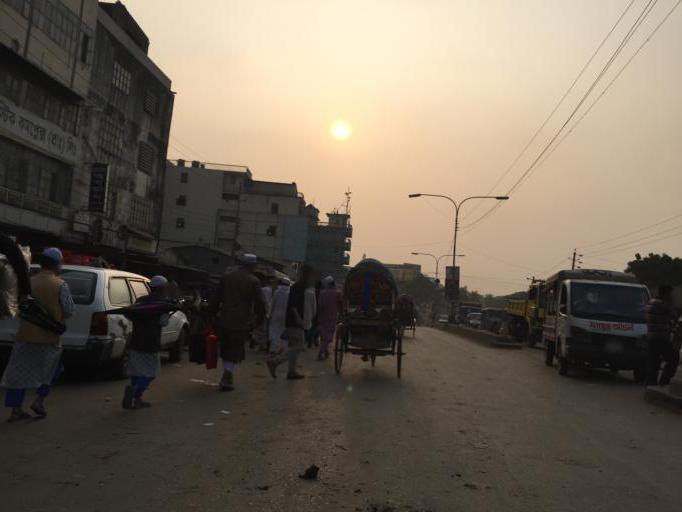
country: BD
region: Dhaka
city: Azimpur
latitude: 23.7968
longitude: 90.3505
